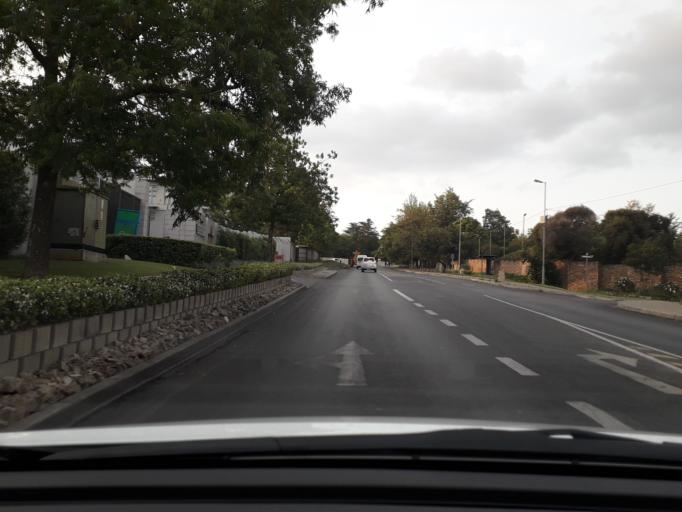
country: ZA
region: Gauteng
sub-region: City of Johannesburg Metropolitan Municipality
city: Midrand
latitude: -26.0585
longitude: 28.0463
